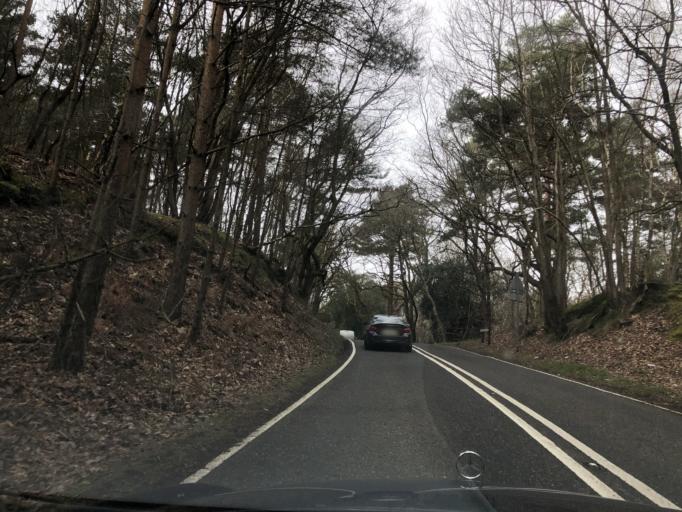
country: GB
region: England
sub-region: Surrey
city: Normandy
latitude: 51.2977
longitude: -0.6996
